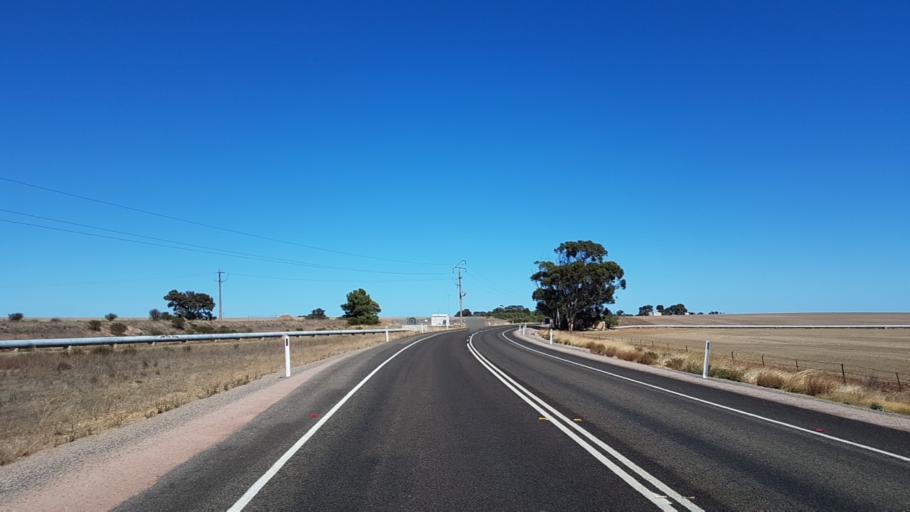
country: AU
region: South Australia
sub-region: Copper Coast
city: Kadina
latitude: -34.0413
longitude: 137.9204
